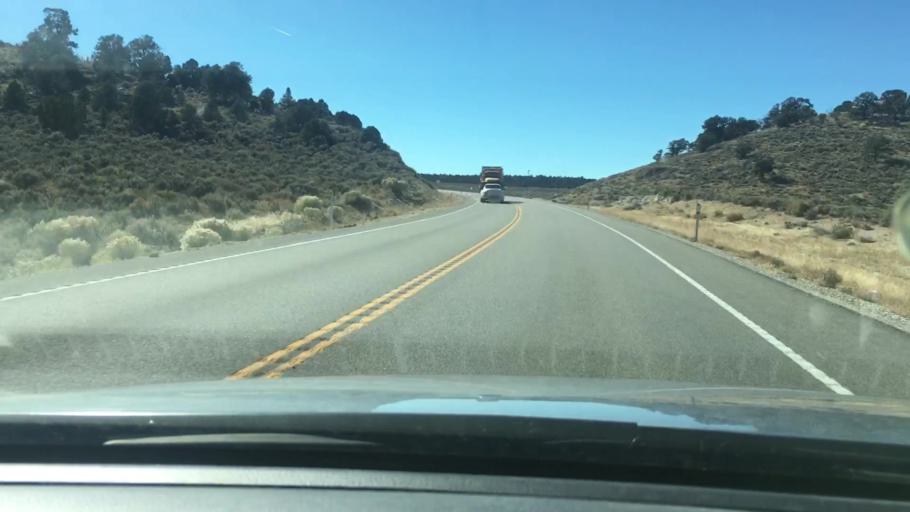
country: US
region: Nevada
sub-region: White Pine County
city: Ely
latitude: 39.2211
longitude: -114.9634
